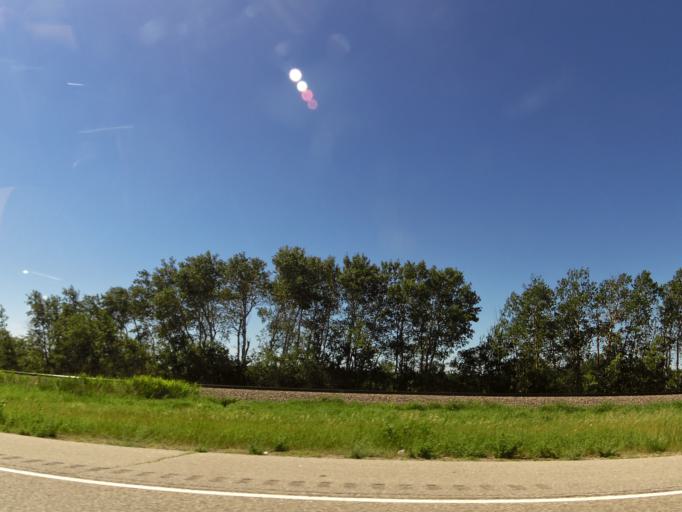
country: US
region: Minnesota
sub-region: Red Lake County
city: Red Lake Falls
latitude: 47.6928
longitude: -96.0979
